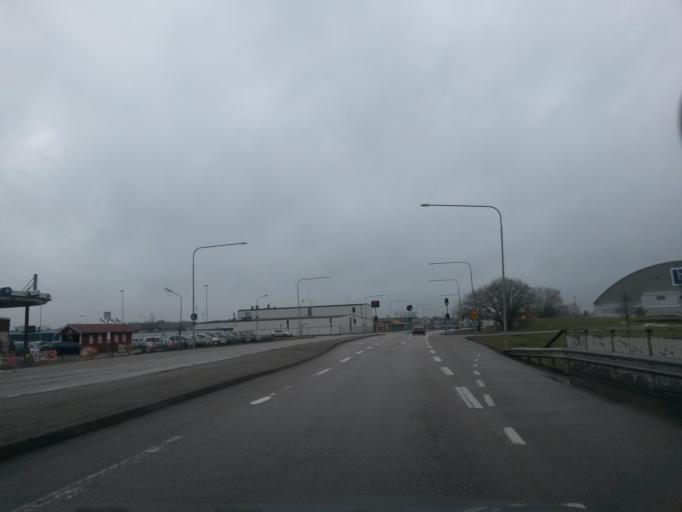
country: SE
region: Vaestra Goetaland
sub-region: Vanersborgs Kommun
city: Vanersborg
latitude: 58.3641
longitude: 12.3360
